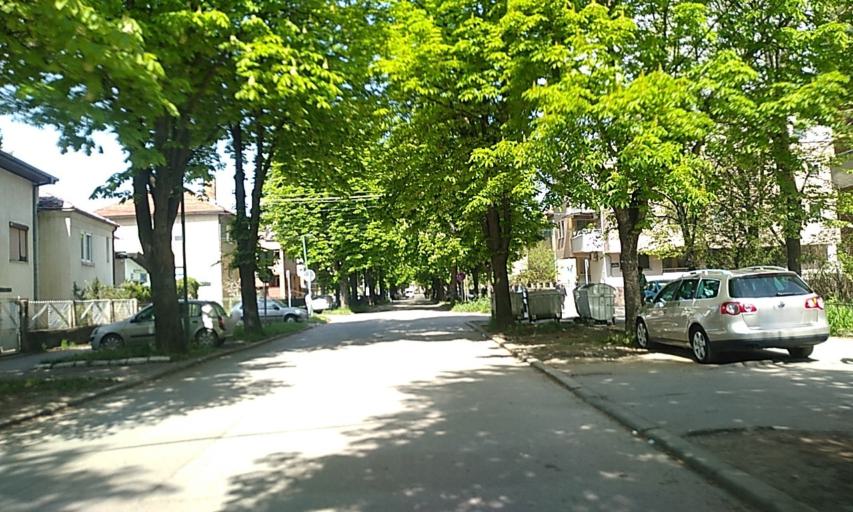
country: RS
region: Central Serbia
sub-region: Nisavski Okrug
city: Nis
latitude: 43.3150
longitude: 21.9221
